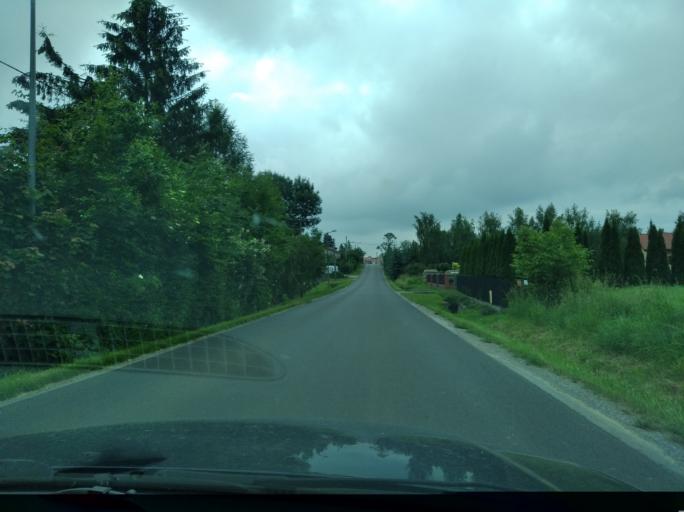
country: PL
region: Subcarpathian Voivodeship
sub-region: Powiat jaroslawski
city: Pawlosiow
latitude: 50.0174
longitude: 22.6416
